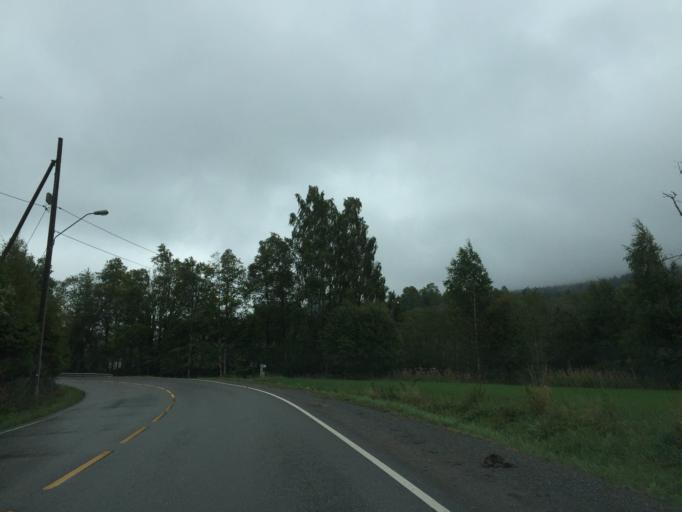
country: NO
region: Akershus
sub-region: Baerum
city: Lysaker
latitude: 59.9916
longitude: 10.6233
